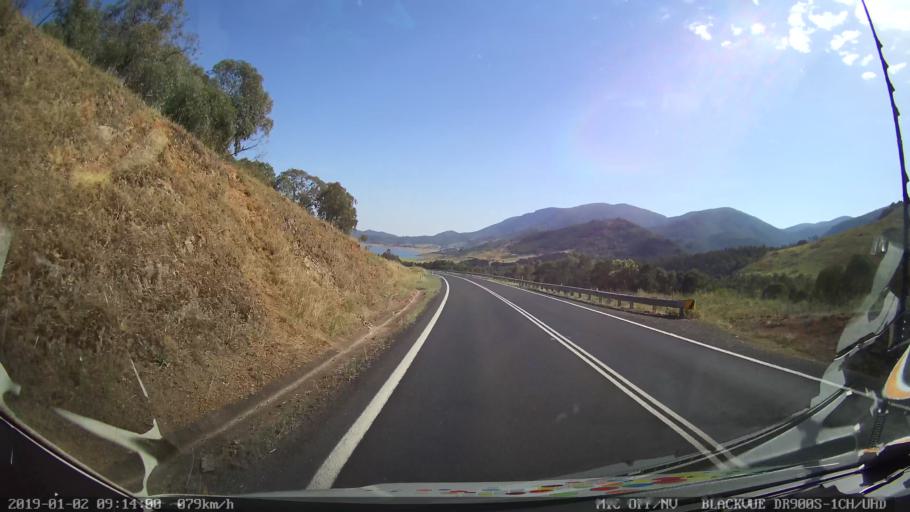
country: AU
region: New South Wales
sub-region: Tumut Shire
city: Tumut
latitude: -35.4827
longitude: 148.2721
